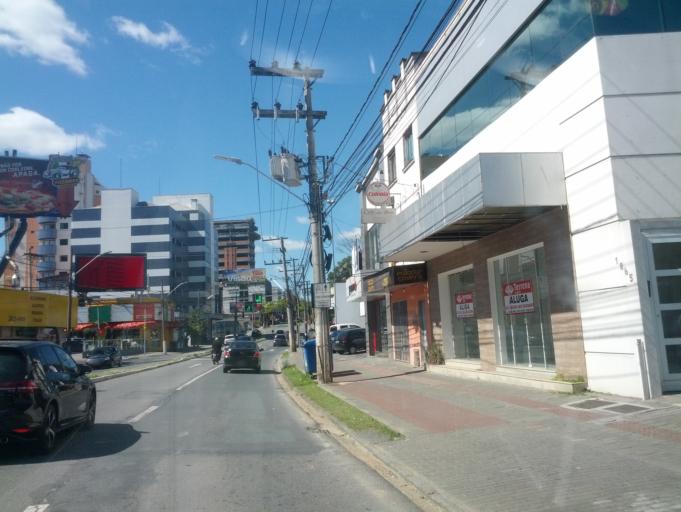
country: BR
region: Santa Catarina
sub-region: Blumenau
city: Blumenau
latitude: -26.9157
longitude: -49.0727
